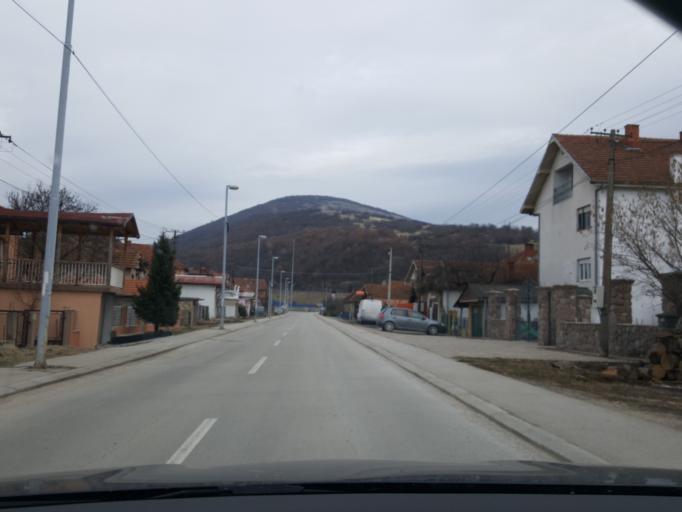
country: RS
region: Central Serbia
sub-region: Pirotski Okrug
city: Dimitrovgrad
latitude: 43.0107
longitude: 22.7568
